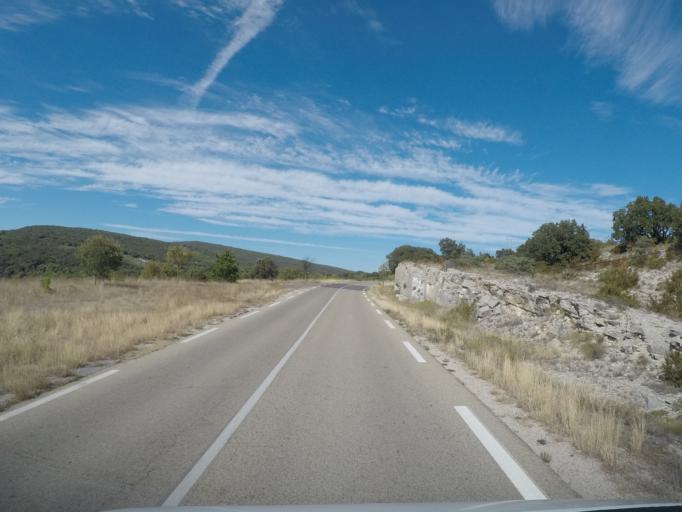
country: FR
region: Languedoc-Roussillon
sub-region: Departement de l'Herault
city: Saint-Martin-de-Londres
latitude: 43.8186
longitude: 3.7446
